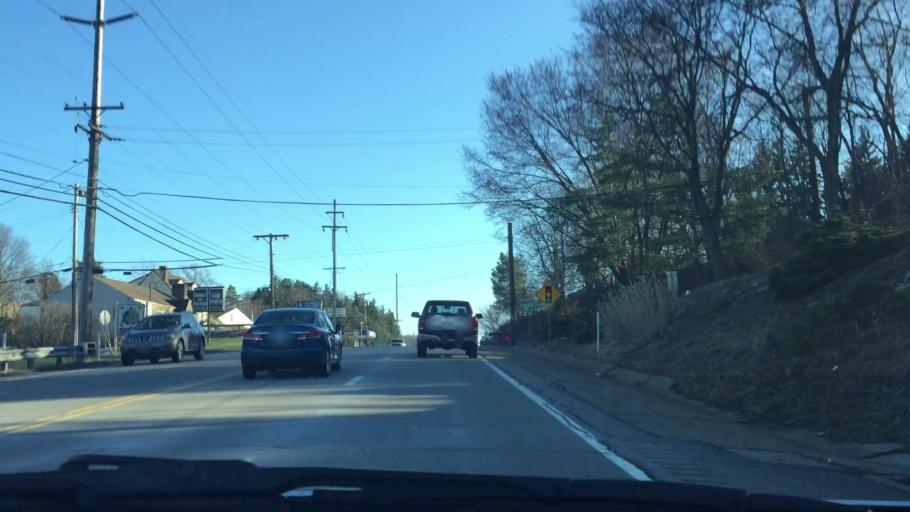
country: US
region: Pennsylvania
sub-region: Allegheny County
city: Franklin Park
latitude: 40.5739
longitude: -80.0371
